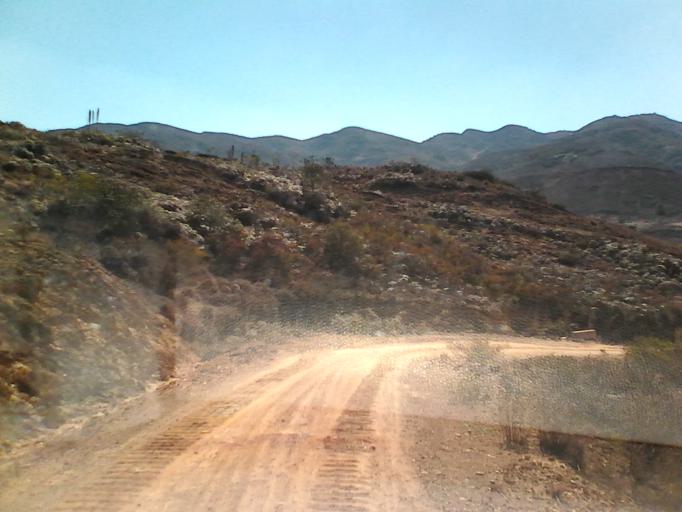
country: CO
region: Boyaca
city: Sachica
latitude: 5.5516
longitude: -73.5651
